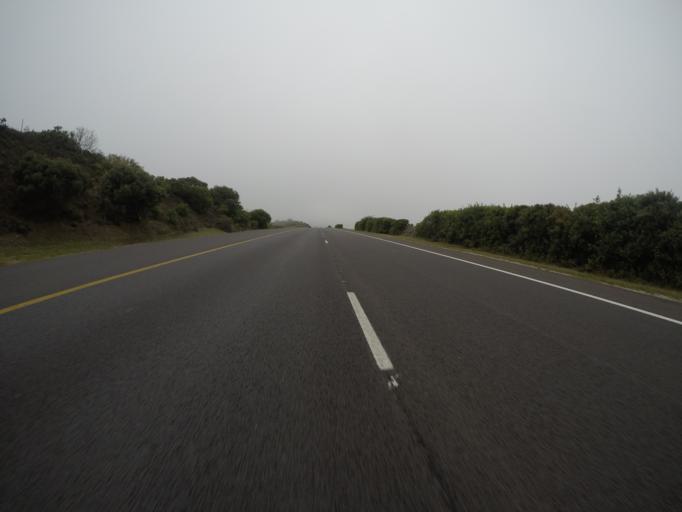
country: ZA
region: Western Cape
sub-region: Eden District Municipality
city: Mossel Bay
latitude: -34.0603
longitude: 22.1946
